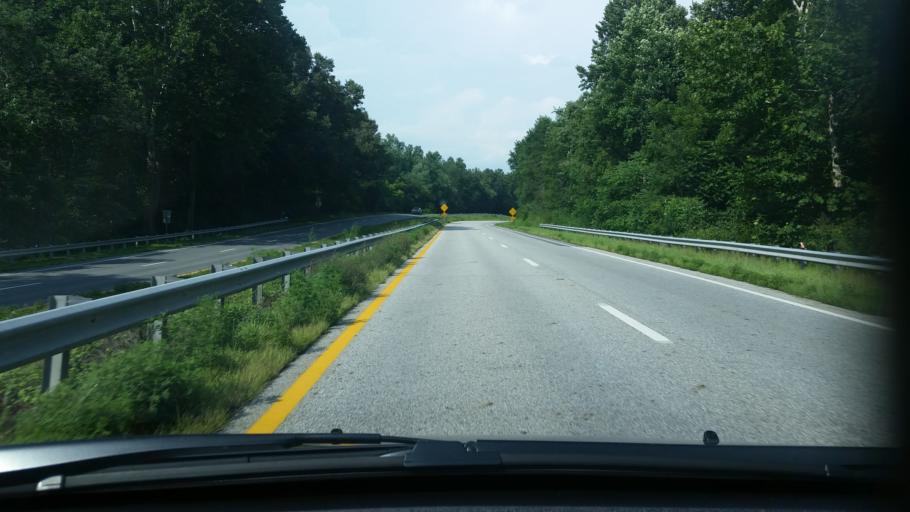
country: US
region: Virginia
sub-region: Nelson County
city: Lovingston
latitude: 37.7414
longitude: -78.8889
